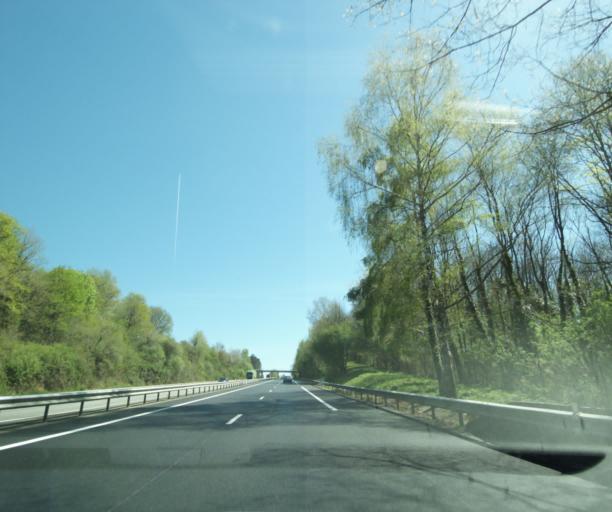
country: FR
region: Limousin
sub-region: Departement de la Haute-Vienne
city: Boisseuil
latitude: 45.7686
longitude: 1.3200
